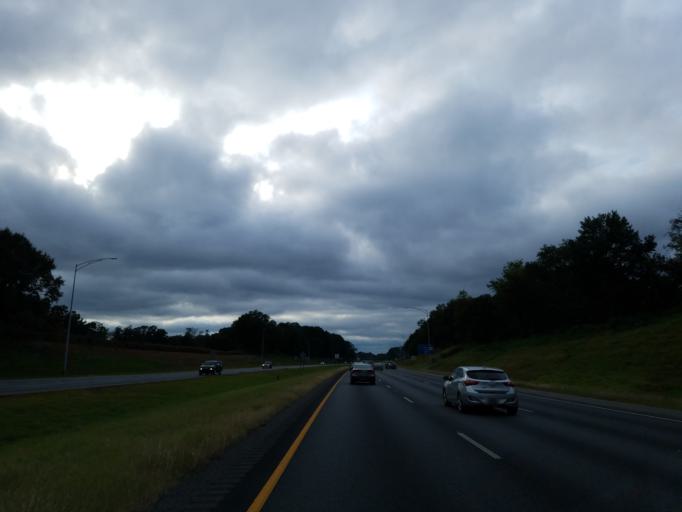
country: US
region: Alabama
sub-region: Tuscaloosa County
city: Tuscaloosa
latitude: 33.1705
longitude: -87.5364
